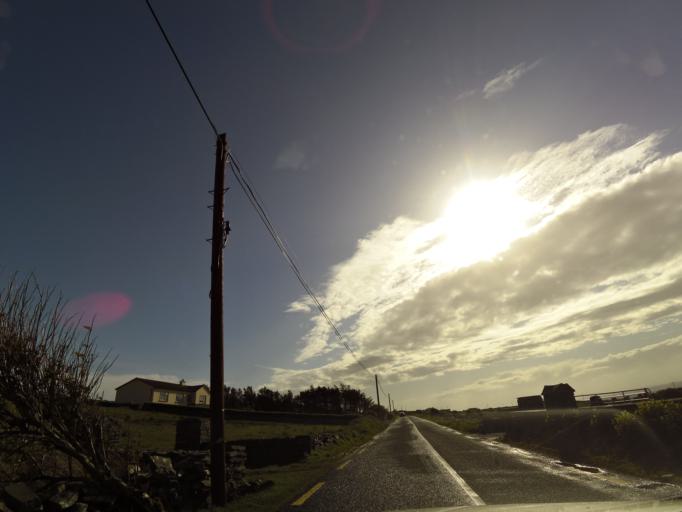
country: IE
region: Connaught
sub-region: County Galway
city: Bearna
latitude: 53.0036
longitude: -9.3718
